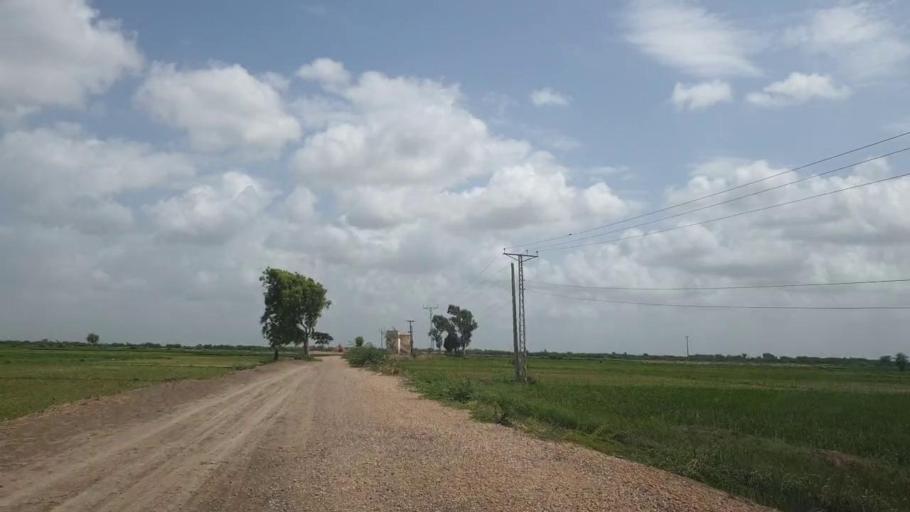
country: PK
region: Sindh
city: Tando Bago
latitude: 24.6484
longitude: 68.9936
